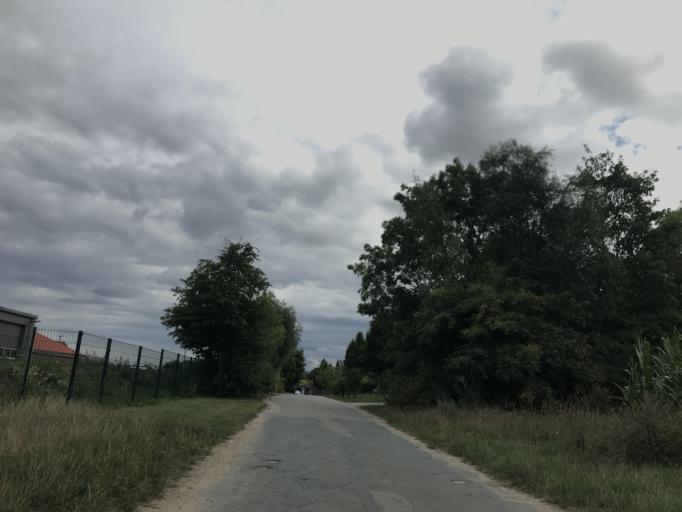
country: DE
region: Lower Saxony
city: Reinstorf
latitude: 53.2357
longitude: 10.5627
